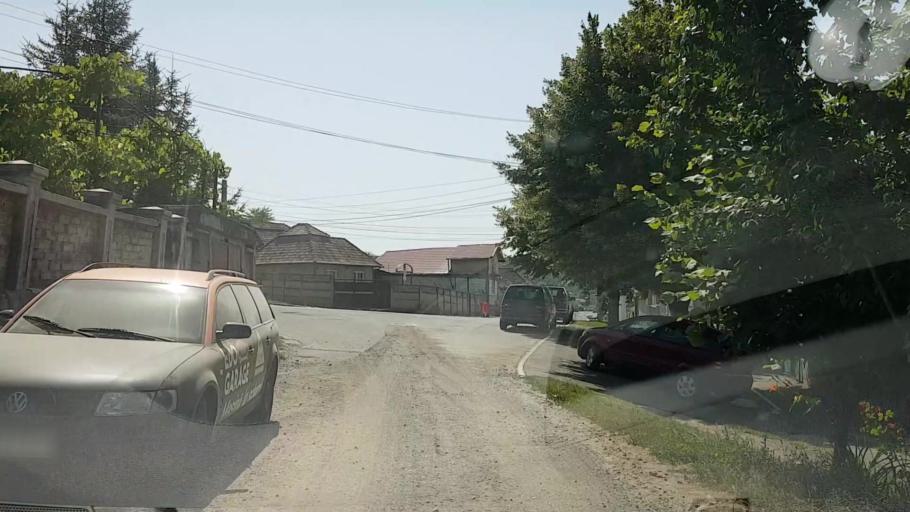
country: RO
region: Cluj
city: Turda
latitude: 46.5778
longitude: 23.7846
